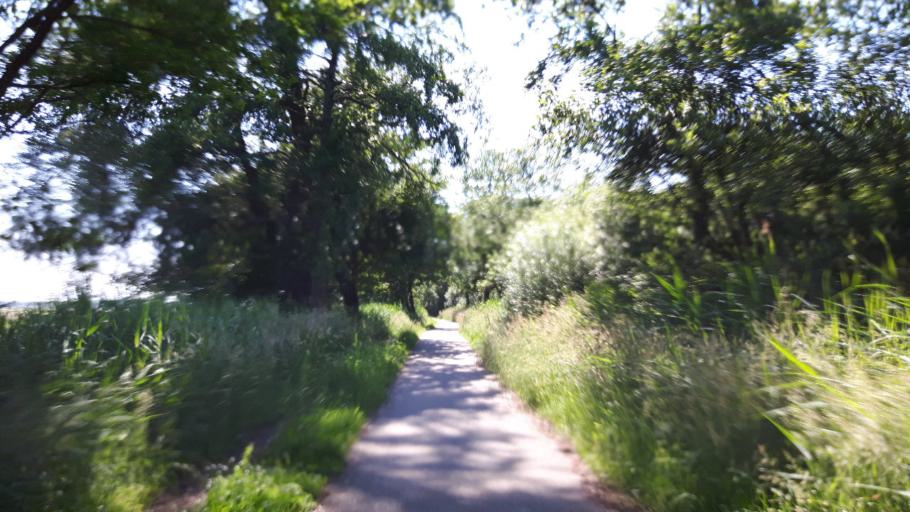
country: NL
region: North Holland
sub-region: Gemeente Wijdemeren
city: Kortenhoef
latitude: 52.2608
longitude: 5.0689
